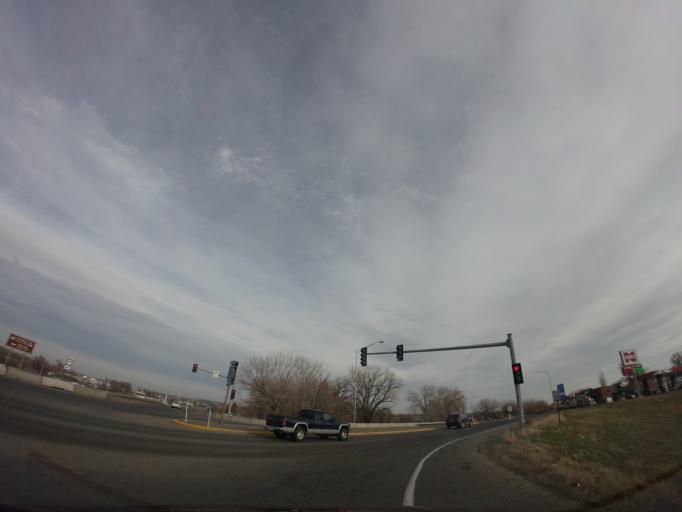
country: US
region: Montana
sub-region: Yellowstone County
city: Billings
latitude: 45.7959
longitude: -108.4562
